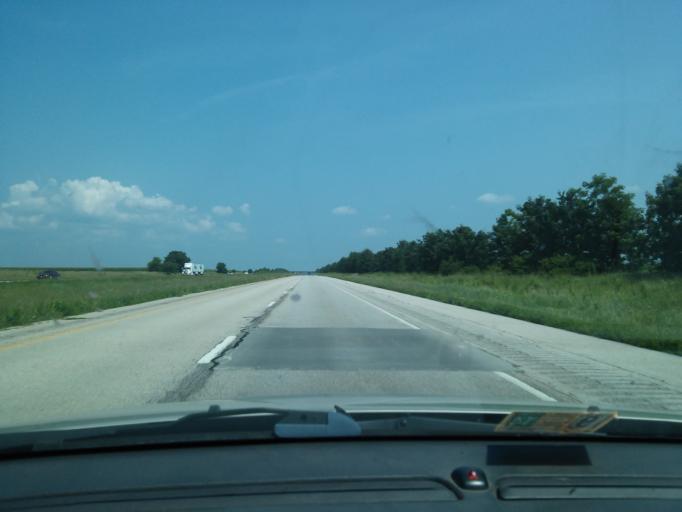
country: US
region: Illinois
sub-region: Sangamon County
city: New Berlin
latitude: 39.7407
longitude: -89.8634
